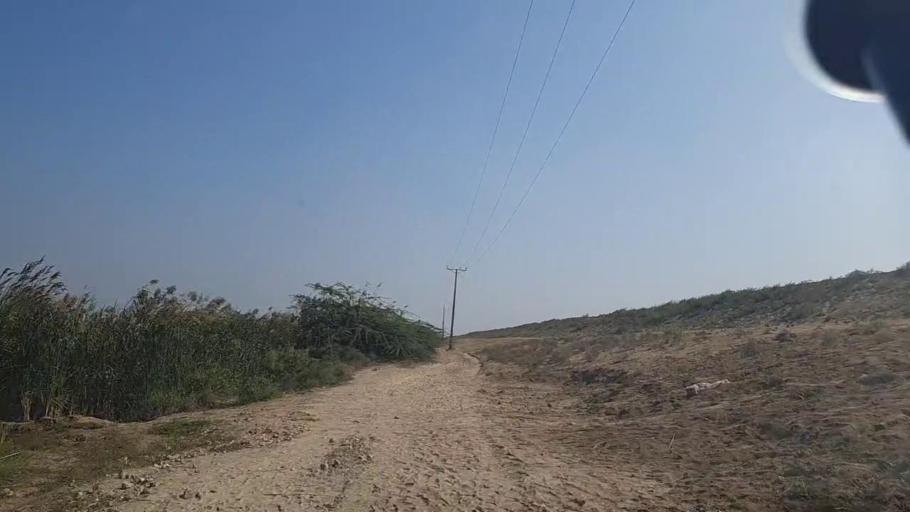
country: PK
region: Sindh
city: Chuhar Jamali
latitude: 24.4618
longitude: 67.8958
